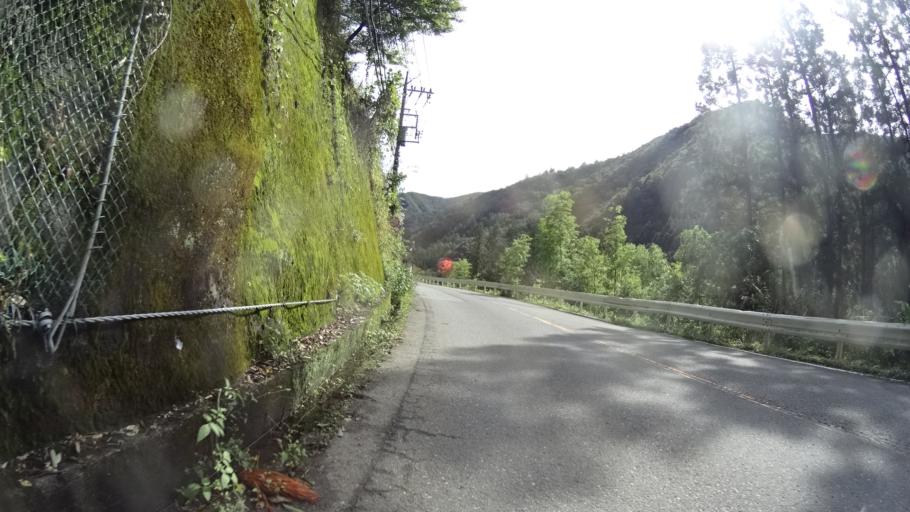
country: JP
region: Yamanashi
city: Otsuki
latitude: 35.7898
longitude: 138.9370
